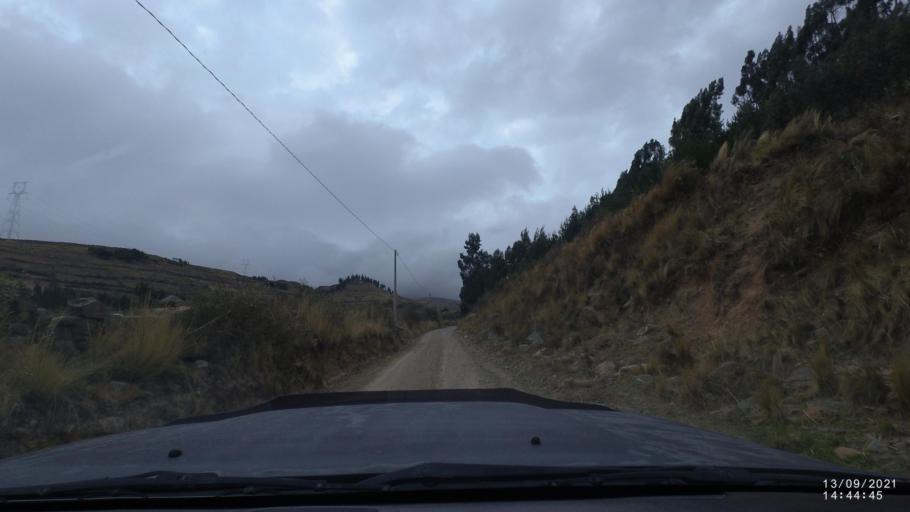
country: BO
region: Cochabamba
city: Colomi
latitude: -17.3566
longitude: -65.8106
